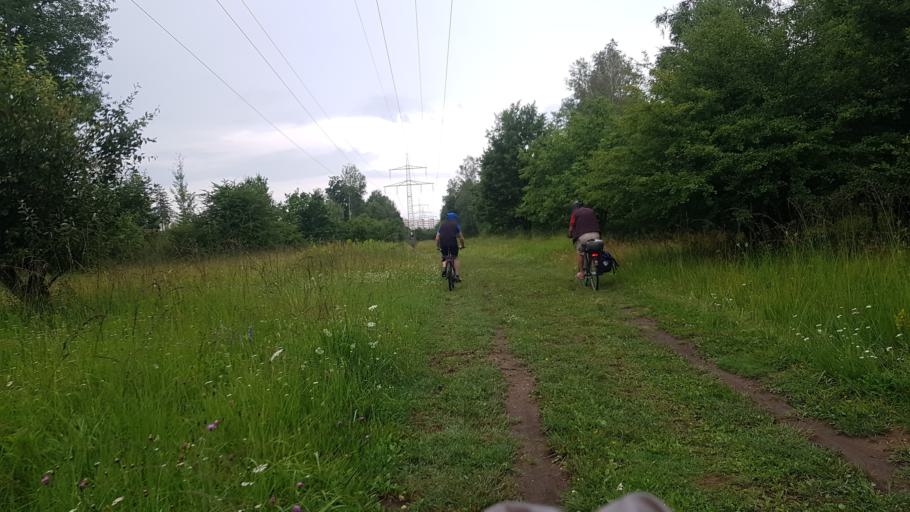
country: DE
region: Bavaria
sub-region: Upper Bavaria
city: Neubiberg
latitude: 48.0962
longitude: 11.6720
